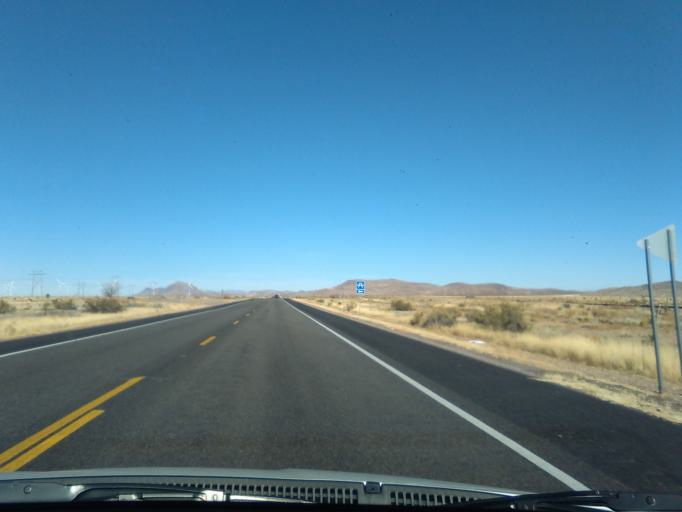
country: US
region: New Mexico
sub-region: Luna County
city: Deming
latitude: 32.4926
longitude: -107.5188
